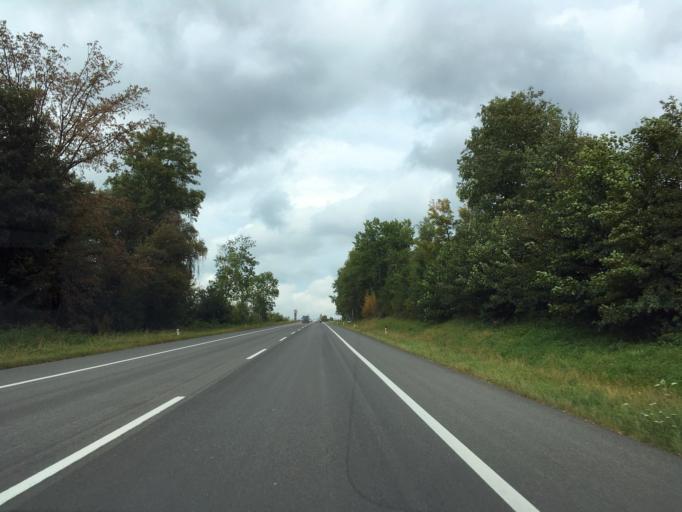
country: AT
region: Styria
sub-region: Politischer Bezirk Hartberg-Fuerstenfeld
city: Friedberg
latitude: 47.4249
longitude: 16.0566
